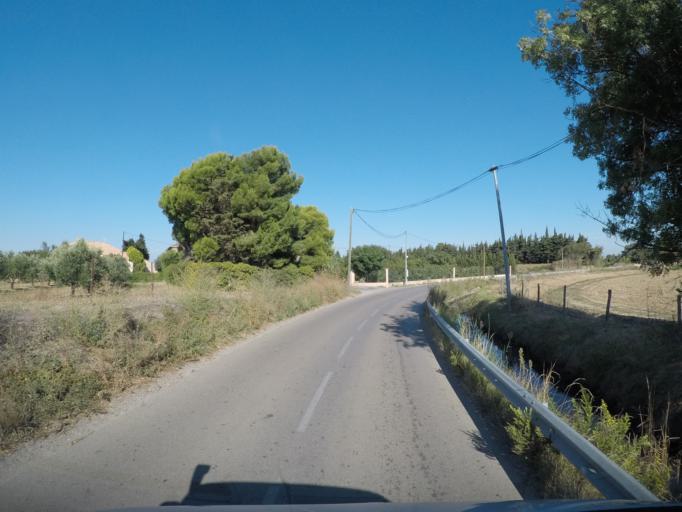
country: FR
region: Languedoc-Roussillon
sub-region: Departement de l'Aude
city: Narbonne
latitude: 43.1627
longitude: 3.0114
